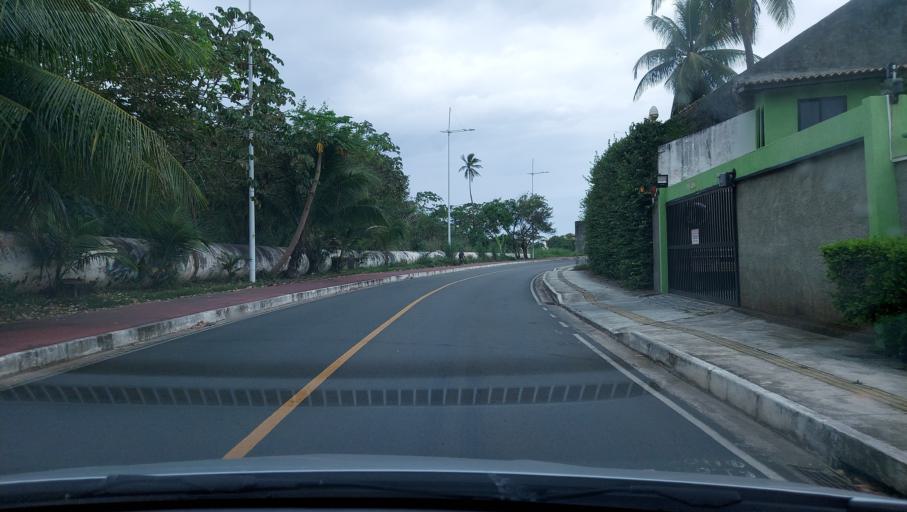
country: BR
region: Bahia
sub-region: Lauro De Freitas
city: Lauro de Freitas
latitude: -12.9538
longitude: -38.3956
